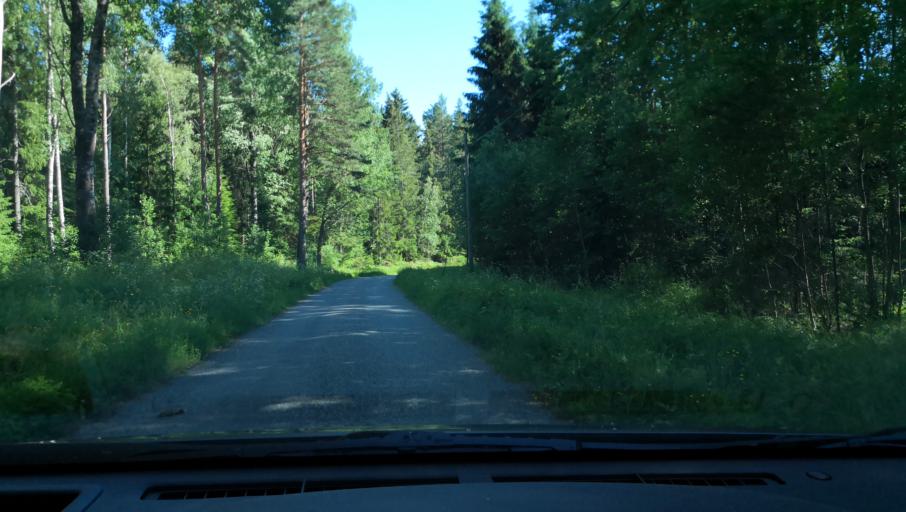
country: SE
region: Soedermanland
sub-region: Eskilstuna Kommun
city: Arla
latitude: 59.3256
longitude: 16.5966
